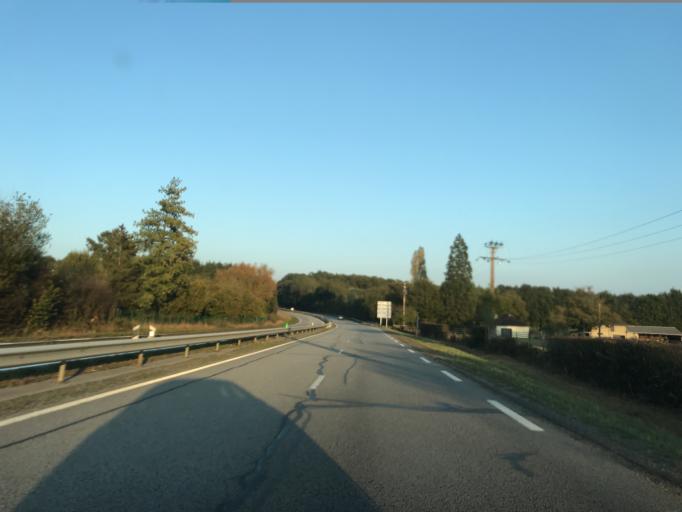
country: FR
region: Pays de la Loire
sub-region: Departement de la Sarthe
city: Mamers
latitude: 48.5077
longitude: 0.3277
